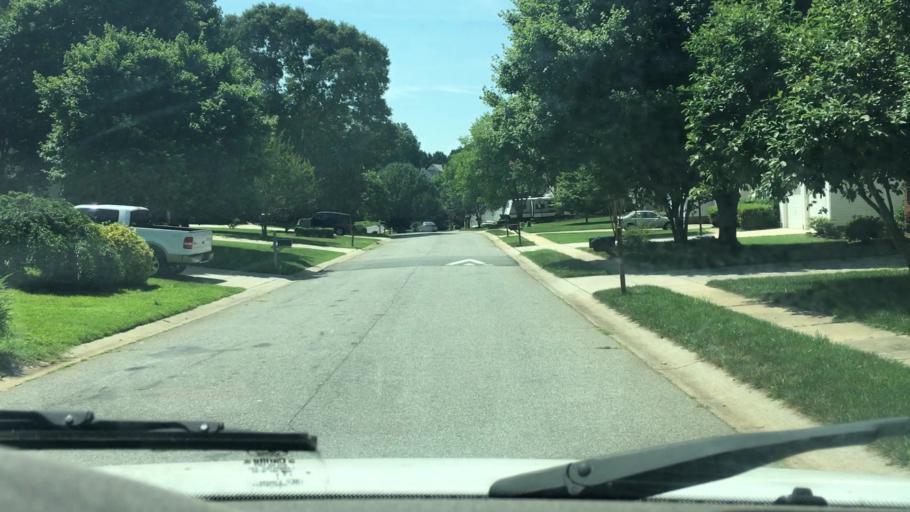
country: US
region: North Carolina
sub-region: Mecklenburg County
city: Huntersville
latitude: 35.4467
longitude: -80.8516
